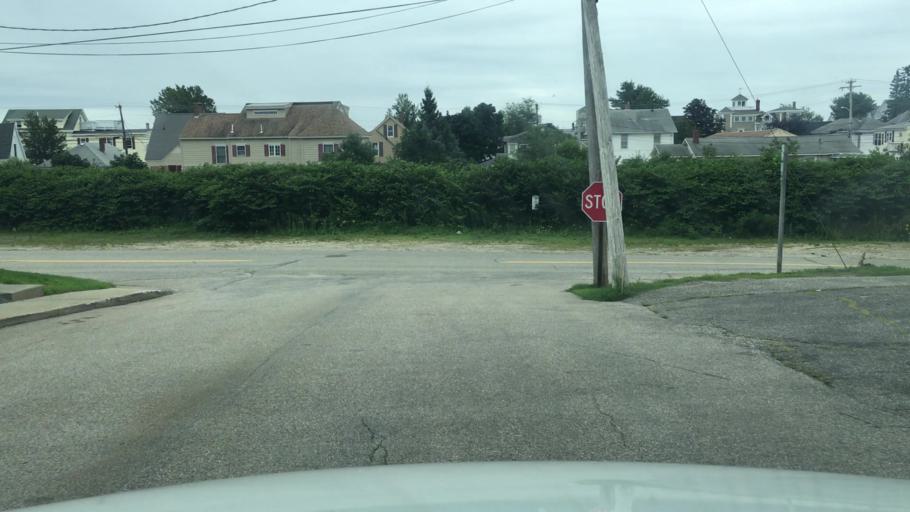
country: US
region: Maine
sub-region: York County
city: Old Orchard Beach
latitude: 43.5091
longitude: -70.3820
